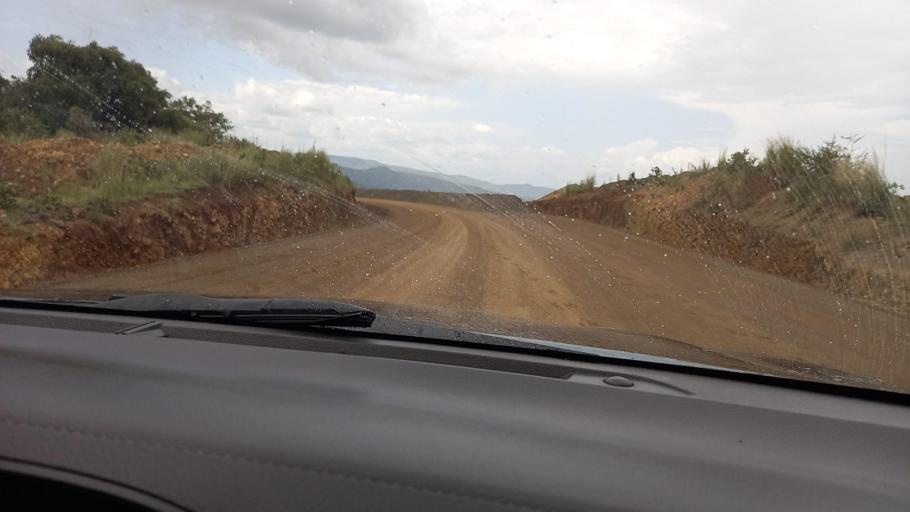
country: ET
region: Southern Nations, Nationalities, and People's Region
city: Mizan Teferi
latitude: 6.1850
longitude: 35.6914
